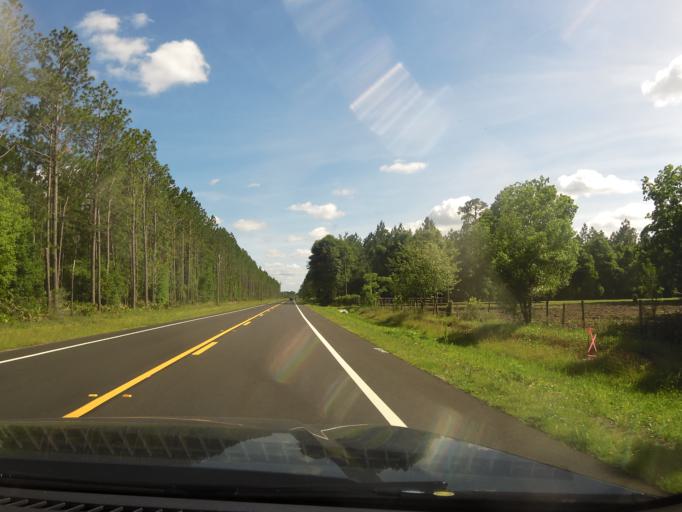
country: US
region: Florida
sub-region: Nassau County
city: Hilliard
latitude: 30.6642
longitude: -81.9035
